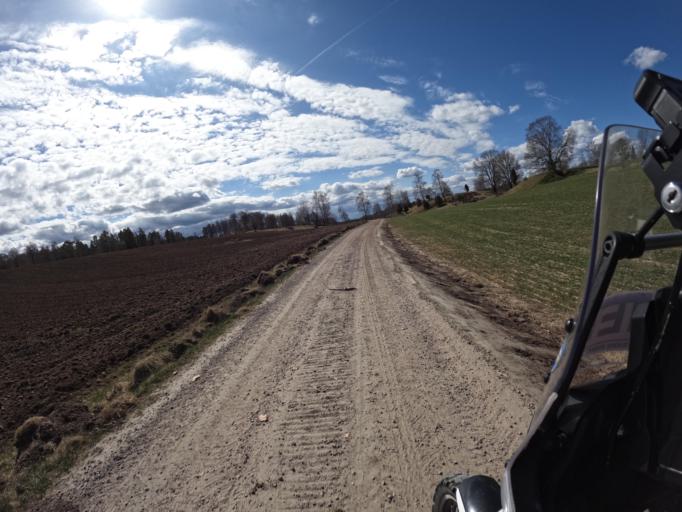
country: SE
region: Vaestra Goetaland
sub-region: Ulricehamns Kommun
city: Ulricehamn
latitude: 57.9268
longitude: 13.4987
